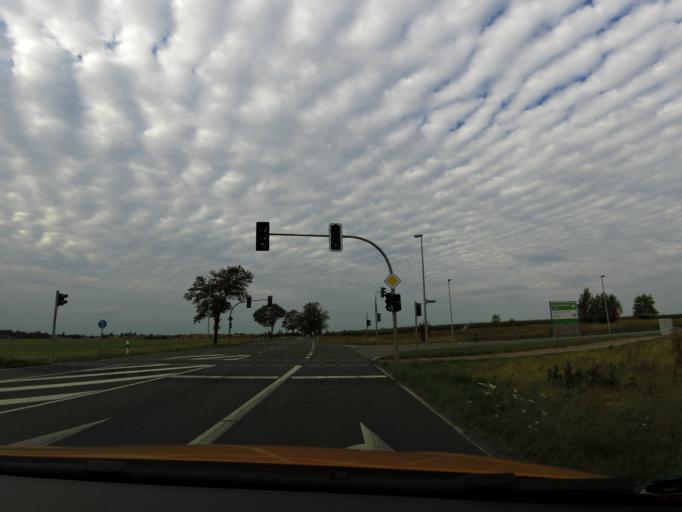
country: DE
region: Brandenburg
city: Brandenburg an der Havel
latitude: 52.3807
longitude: 12.5943
